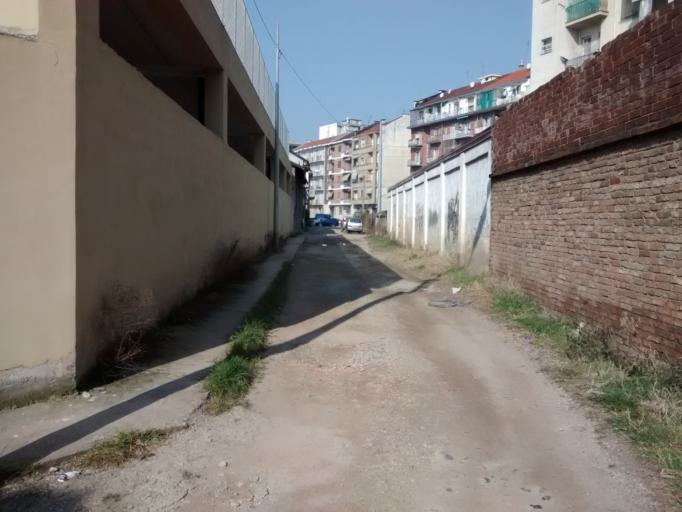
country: IT
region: Piedmont
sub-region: Provincia di Torino
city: Turin
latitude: 45.1013
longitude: 7.6654
